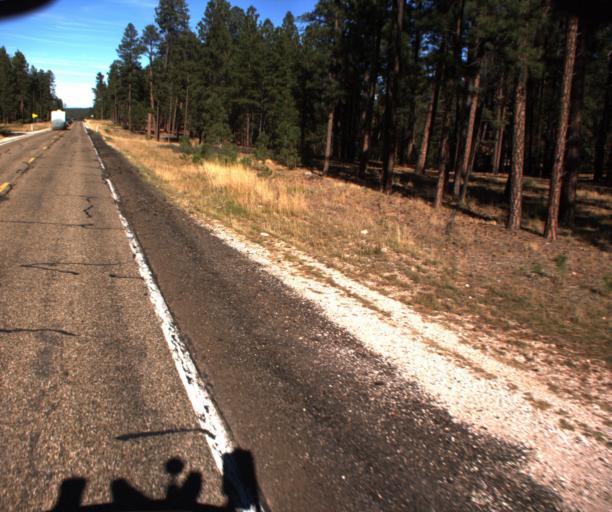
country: US
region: Arizona
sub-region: Coconino County
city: Fredonia
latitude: 36.7233
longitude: -112.2001
